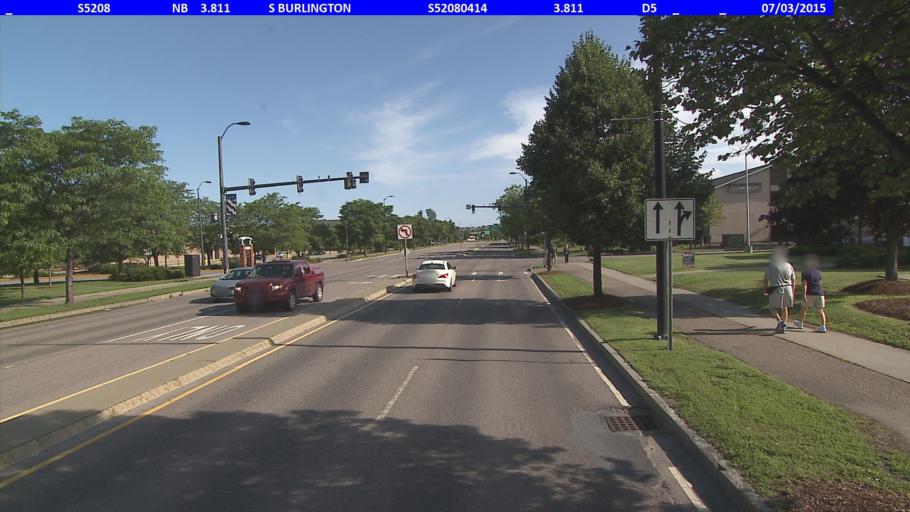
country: US
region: Vermont
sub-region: Chittenden County
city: South Burlington
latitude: 44.4650
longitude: -73.1809
